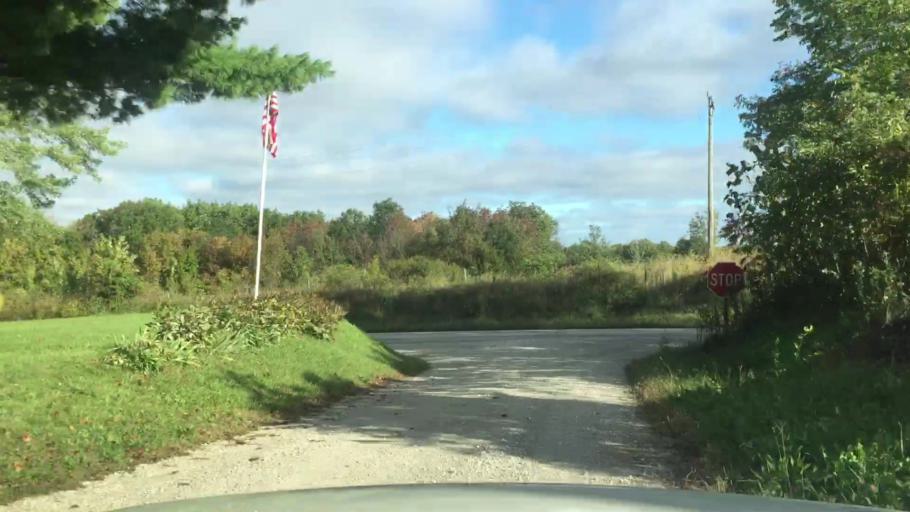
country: US
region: Missouri
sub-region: Howard County
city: New Franklin
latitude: 39.1049
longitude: -92.7792
